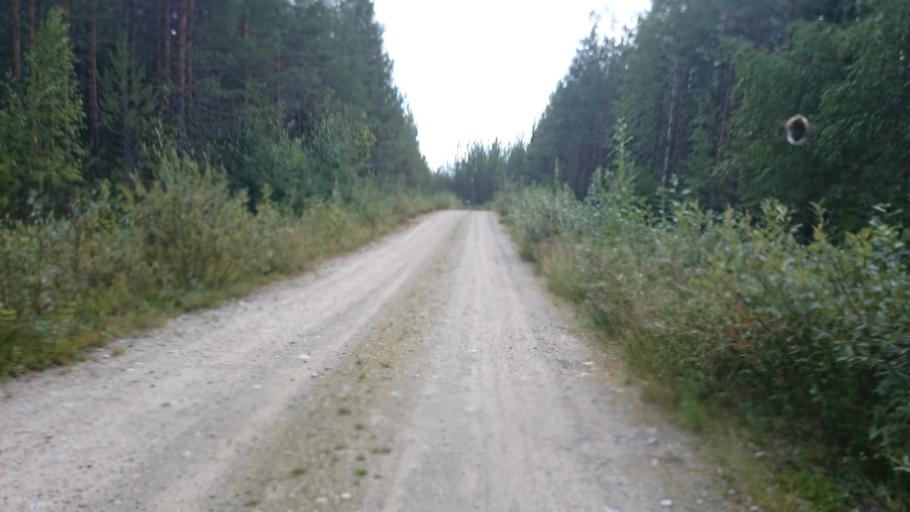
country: FI
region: Kainuu
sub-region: Kehys-Kainuu
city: Kuhmo
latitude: 64.4251
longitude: 29.8193
